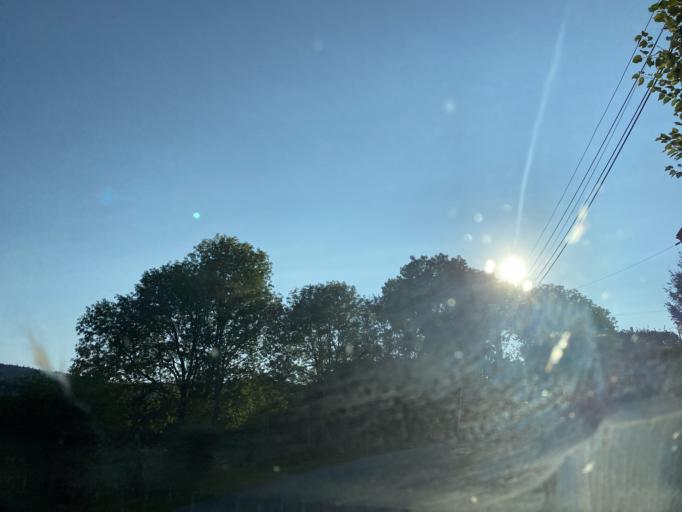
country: FR
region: Rhone-Alpes
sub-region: Departement de la Loire
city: Noiretable
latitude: 45.8056
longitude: 3.7624
